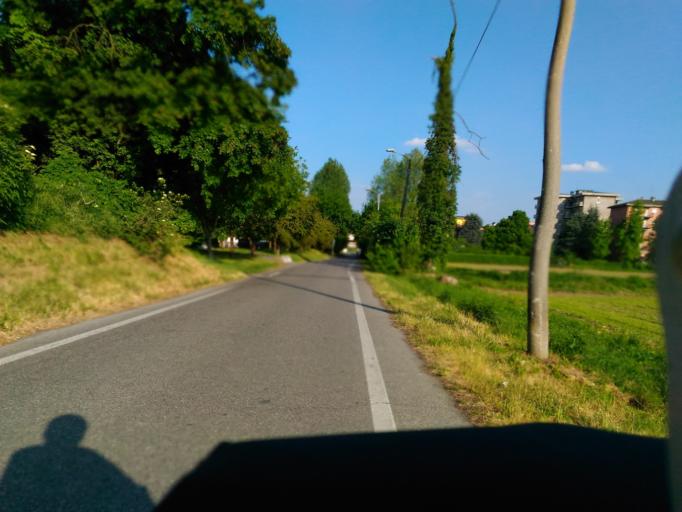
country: IT
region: Lombardy
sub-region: Provincia di Lodi
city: Lodi
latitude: 45.3175
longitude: 9.4878
